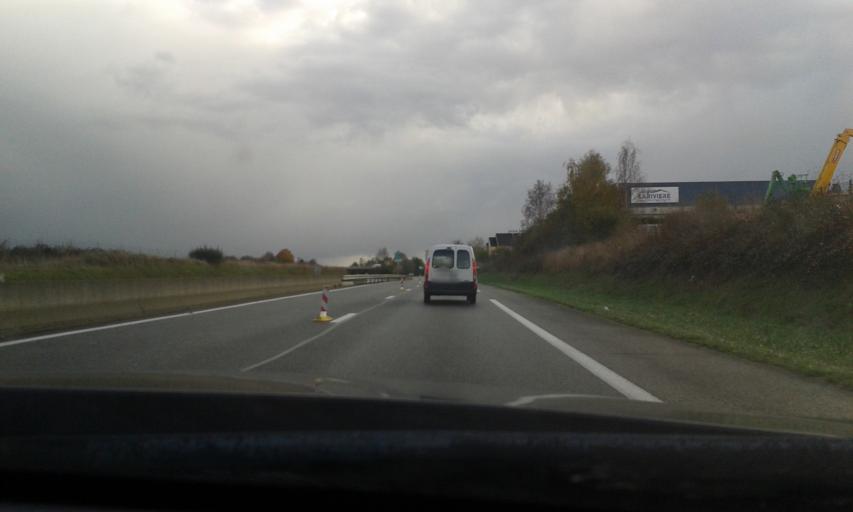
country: FR
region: Haute-Normandie
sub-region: Departement de l'Eure
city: Gravigny
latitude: 49.0333
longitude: 1.1863
